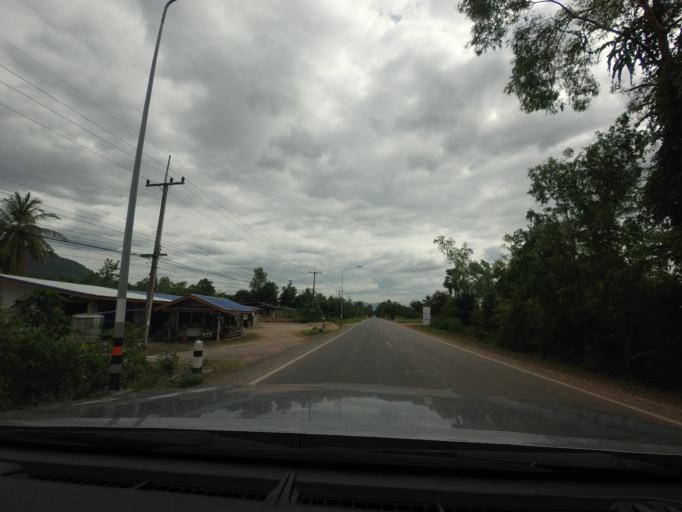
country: TH
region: Phitsanulok
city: Noen Maprang
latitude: 16.7055
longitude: 100.5842
